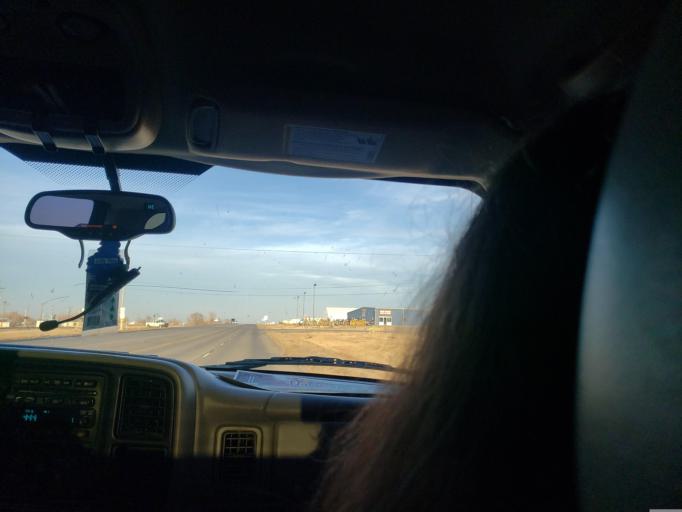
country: US
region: Oklahoma
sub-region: Texas County
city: Guymon
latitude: 36.6969
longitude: -101.4578
